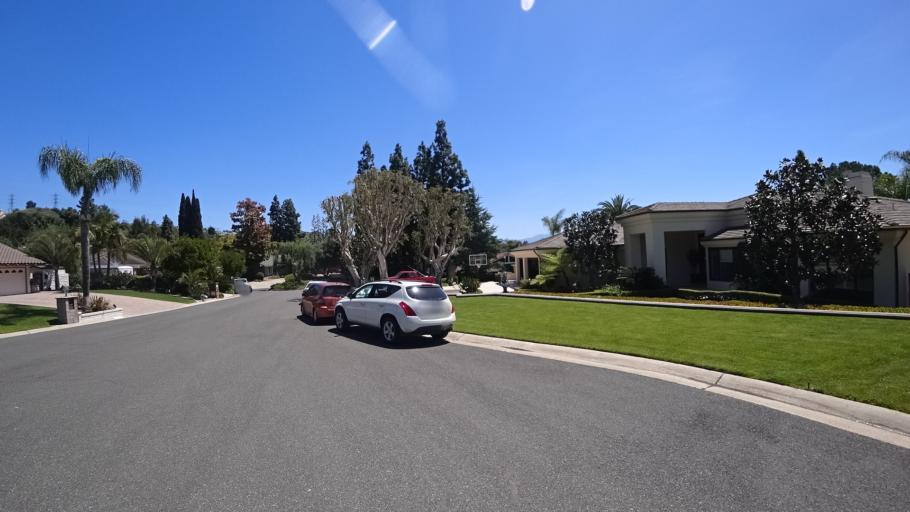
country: US
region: California
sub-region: Orange County
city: Villa Park
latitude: 33.8291
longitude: -117.8043
